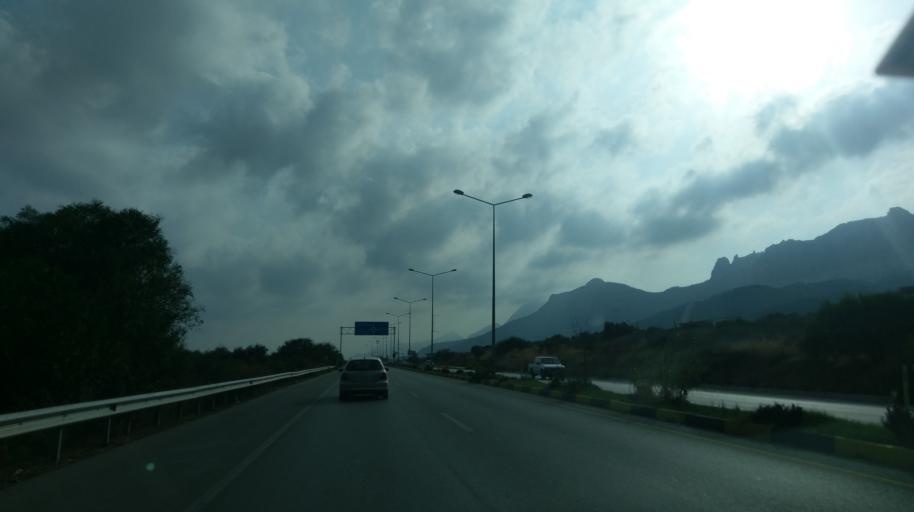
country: CY
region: Keryneia
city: Kyrenia
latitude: 35.3322
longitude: 33.2714
